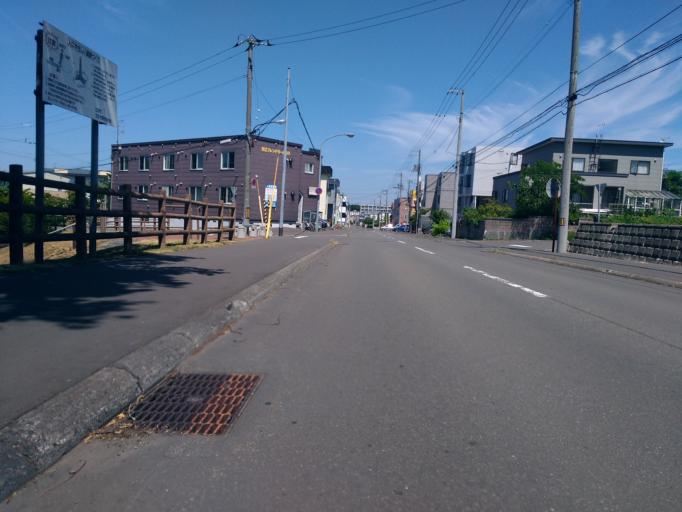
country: JP
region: Hokkaido
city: Ebetsu
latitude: 43.0666
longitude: 141.4983
